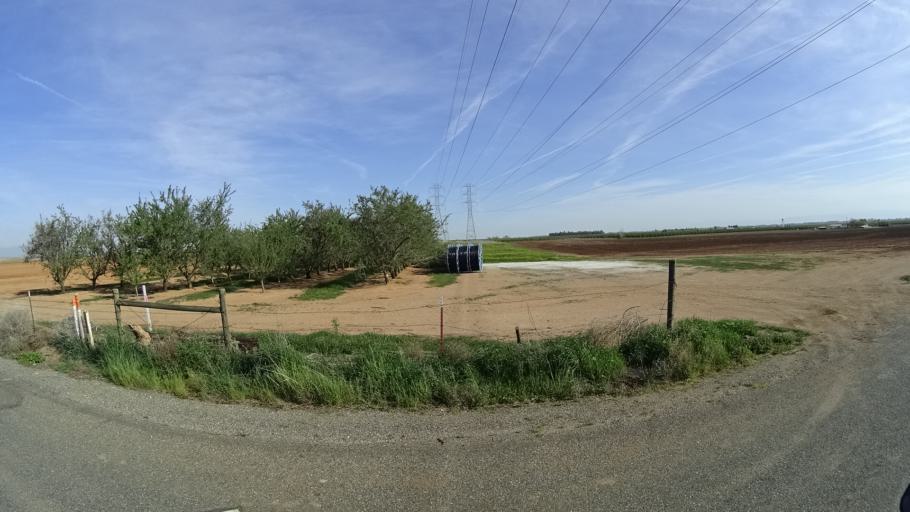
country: US
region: California
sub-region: Glenn County
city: Orland
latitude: 39.6683
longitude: -122.2650
